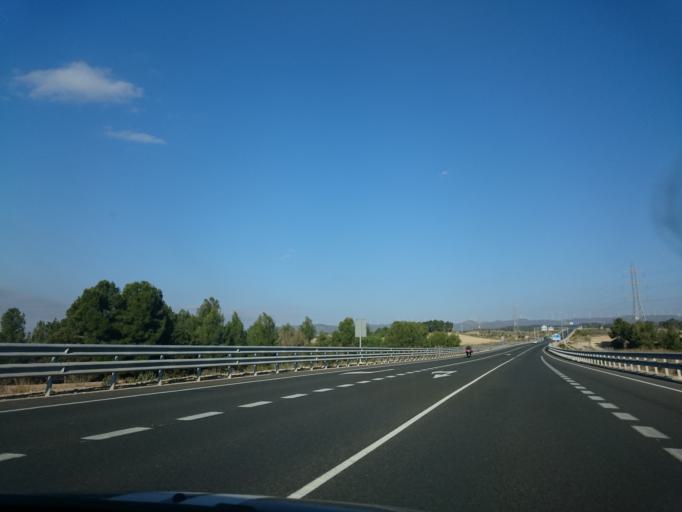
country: ES
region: Catalonia
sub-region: Provincia de Barcelona
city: Odena
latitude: 41.5836
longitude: 1.6658
